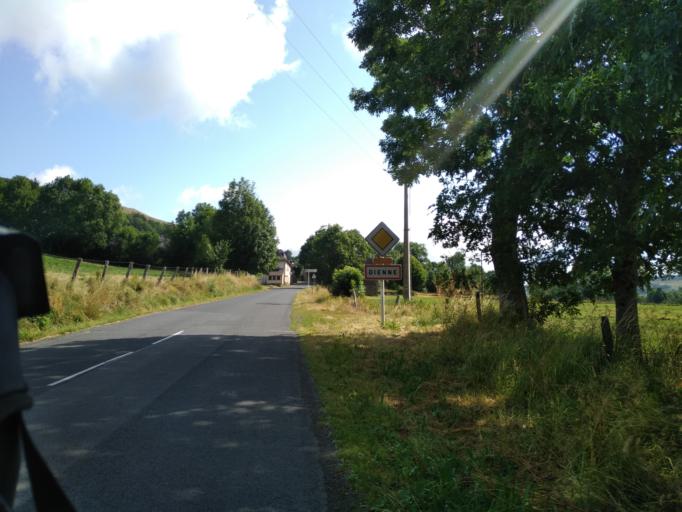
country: FR
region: Auvergne
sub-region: Departement du Cantal
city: Murat
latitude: 45.1565
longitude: 2.7848
